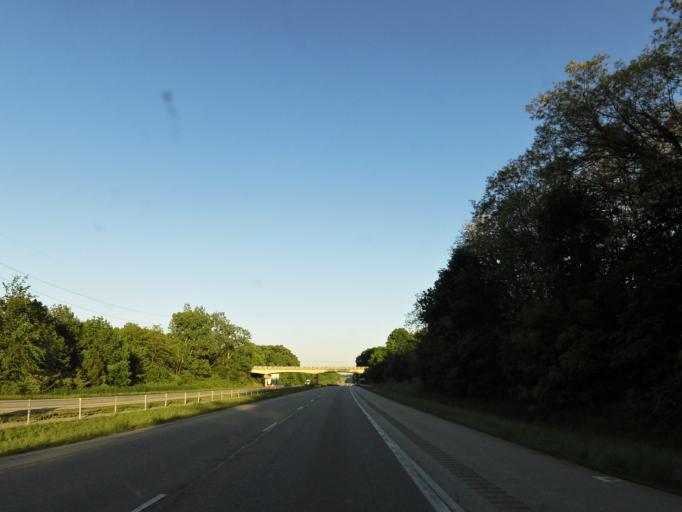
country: US
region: Illinois
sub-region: Vermilion County
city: Catlin
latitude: 40.1184
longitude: -87.6997
